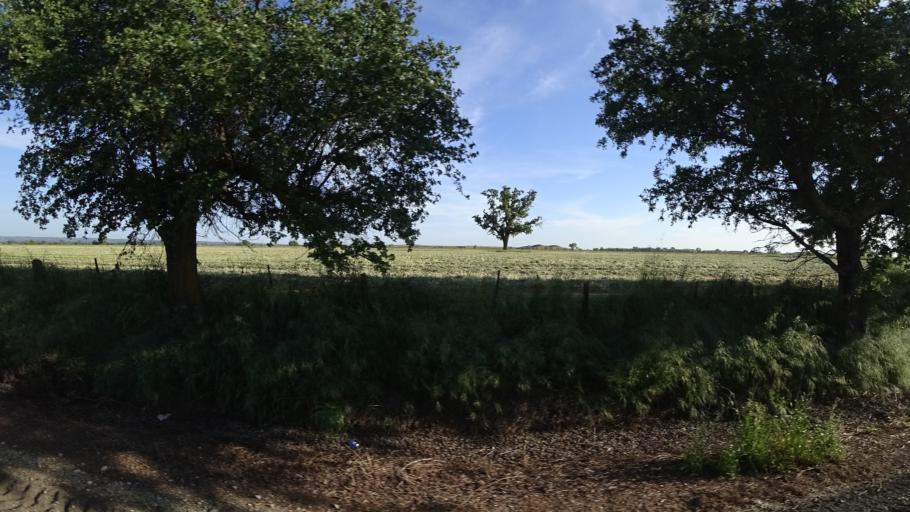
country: US
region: California
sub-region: Placer County
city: Lincoln
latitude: 38.9265
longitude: -121.3000
